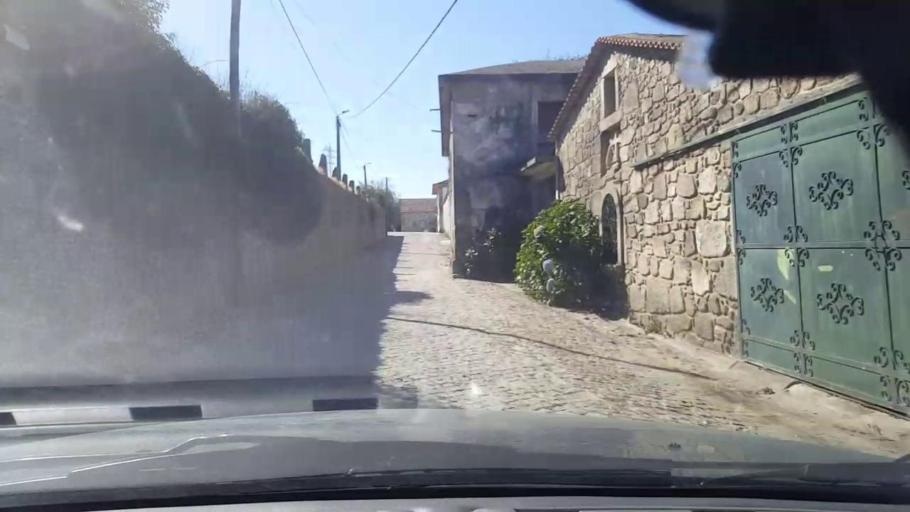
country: PT
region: Porto
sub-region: Maia
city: Gemunde
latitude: 41.2918
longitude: -8.6490
